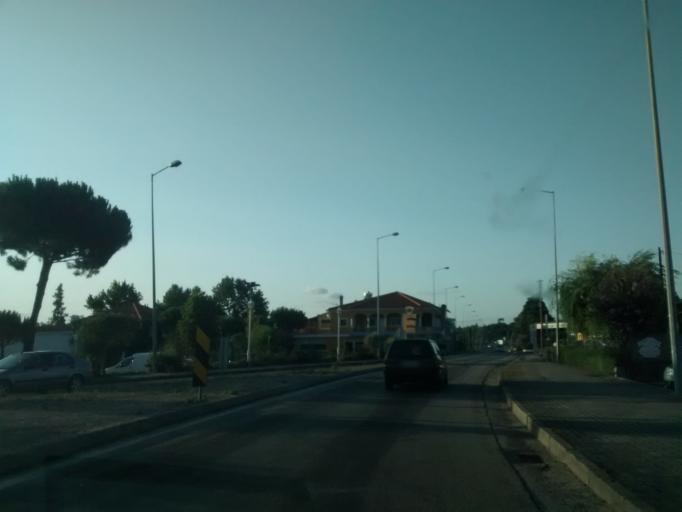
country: PT
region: Aveiro
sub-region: Mealhada
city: Mealhada
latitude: 40.3893
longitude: -8.4506
